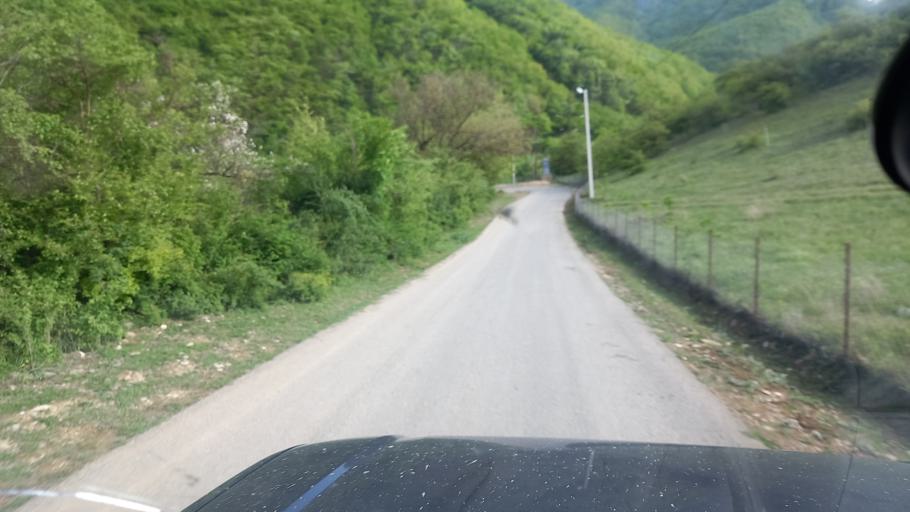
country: RU
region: Dagestan
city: Khuchni
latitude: 41.9657
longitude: 47.9585
